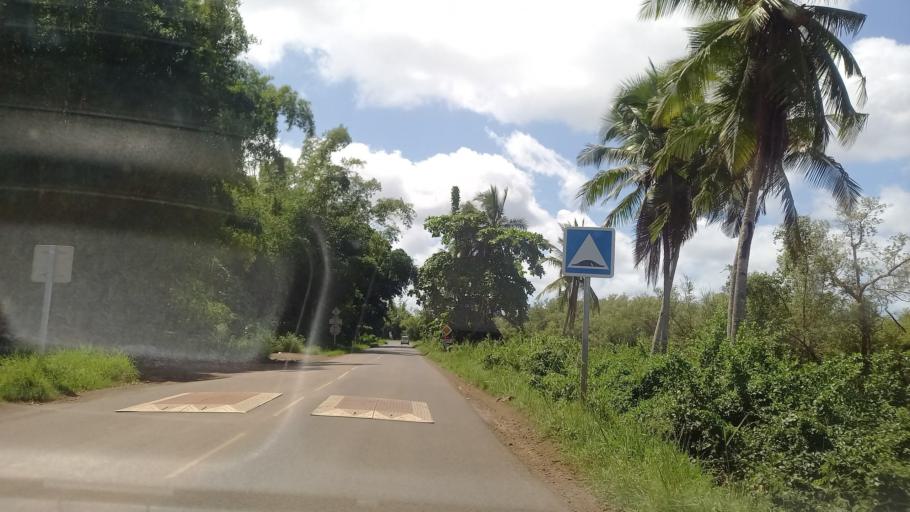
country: YT
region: Bandraboua
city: Bandraboua
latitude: -12.7226
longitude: 45.1282
